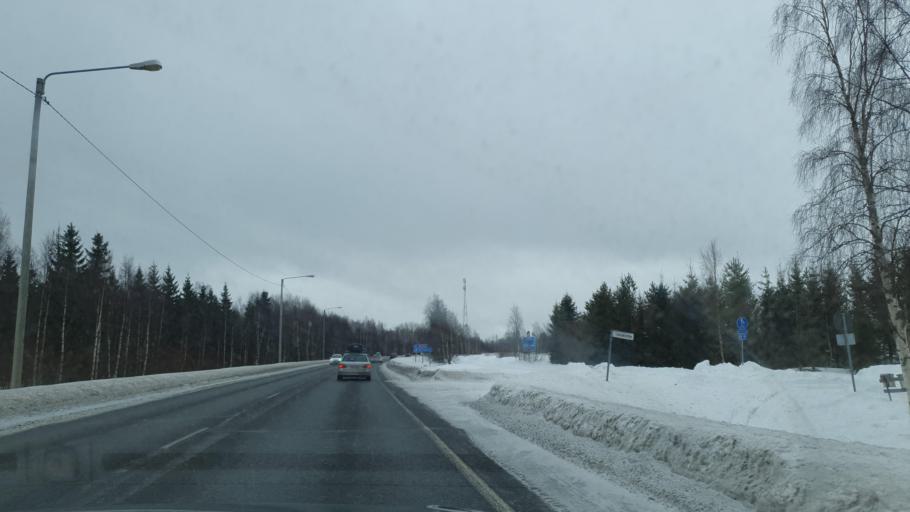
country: FI
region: Lapland
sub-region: Kemi-Tornio
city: Tornio
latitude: 65.8745
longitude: 24.1626
